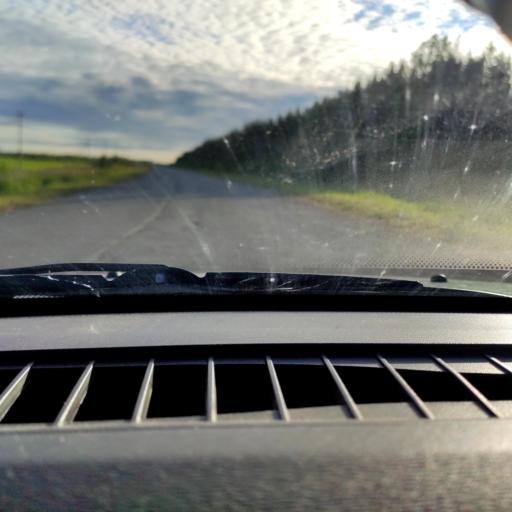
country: RU
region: Perm
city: Uinskoye
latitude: 57.1017
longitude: 56.6549
